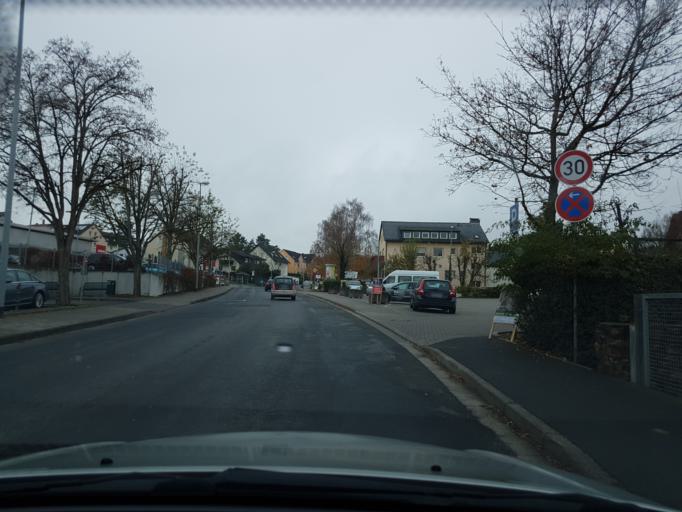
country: DE
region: Hesse
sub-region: Regierungsbezirk Darmstadt
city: Kiedrich
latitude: 50.0400
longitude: 8.0827
